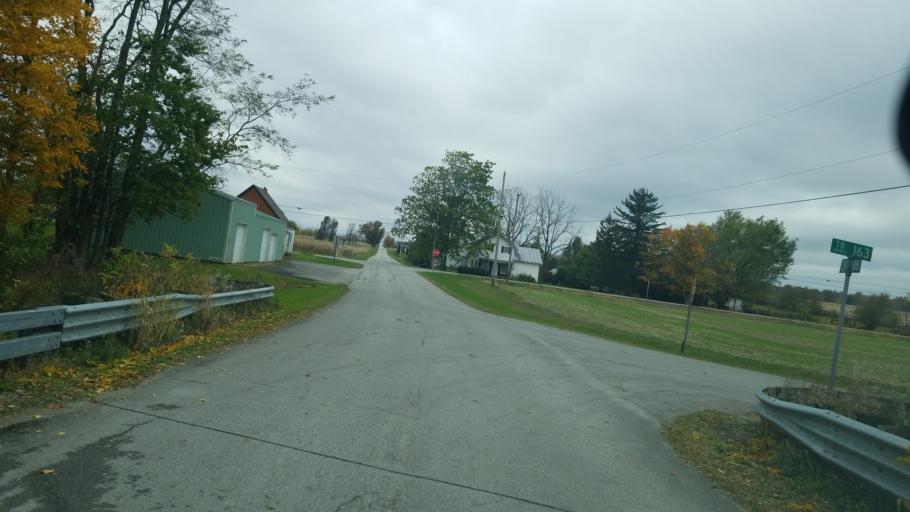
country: US
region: Ohio
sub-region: Seneca County
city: Tiffin
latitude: 41.0666
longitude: -83.0132
